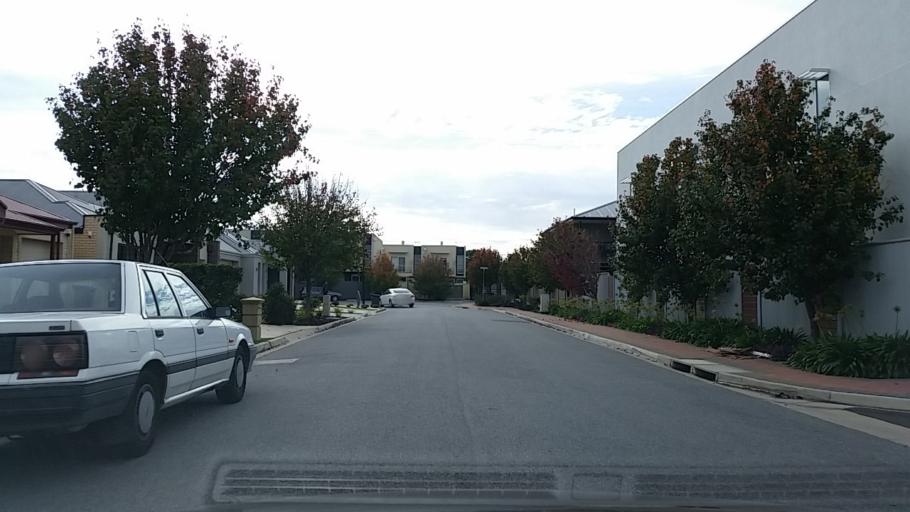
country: AU
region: South Australia
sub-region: Charles Sturt
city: Findon
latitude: -34.9032
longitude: 138.5284
